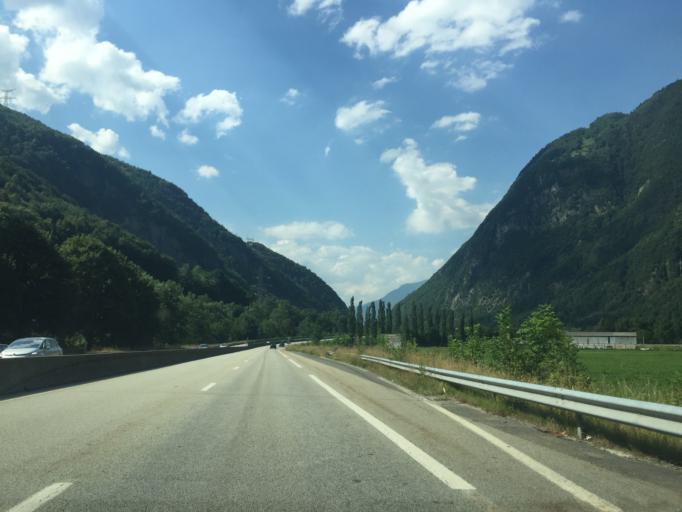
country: FR
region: Rhone-Alpes
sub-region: Departement de la Savoie
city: Aigueblanche
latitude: 45.5573
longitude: 6.4670
